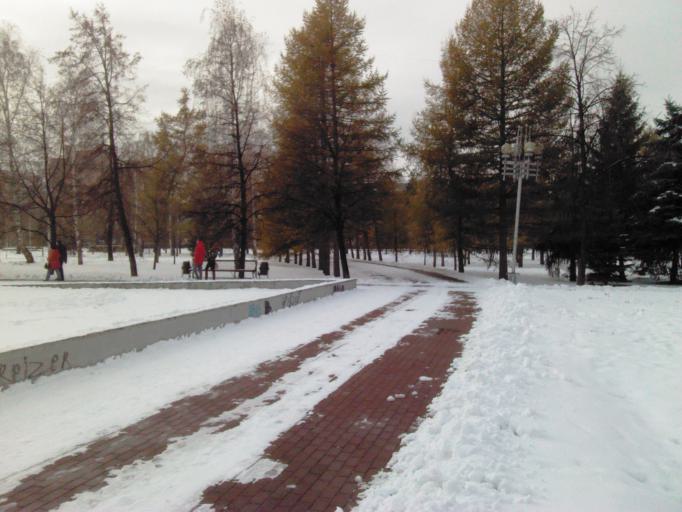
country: RU
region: Chelyabinsk
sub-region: Gorod Chelyabinsk
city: Chelyabinsk
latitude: 55.1621
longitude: 61.3913
